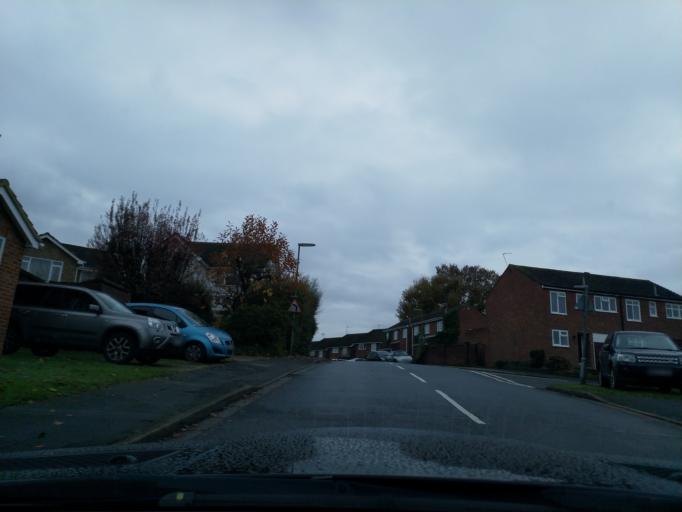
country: GB
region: England
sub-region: Surrey
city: Frimley
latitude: 51.3148
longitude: -0.7294
